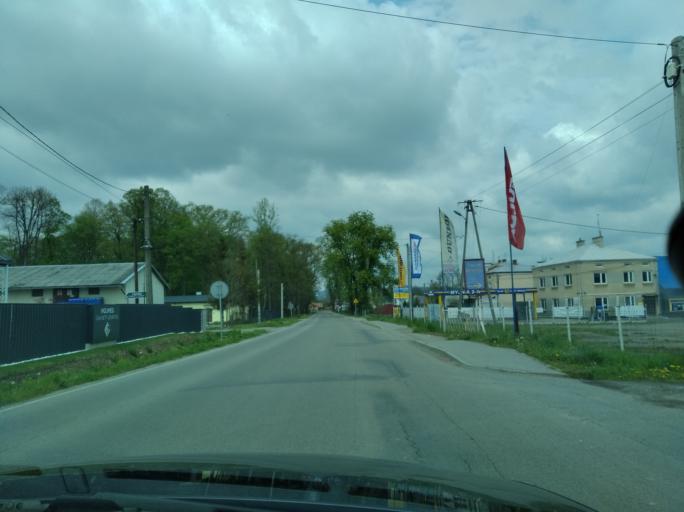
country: PL
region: Subcarpathian Voivodeship
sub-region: Powiat brzozowski
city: Haczow
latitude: 49.6690
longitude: 21.8963
